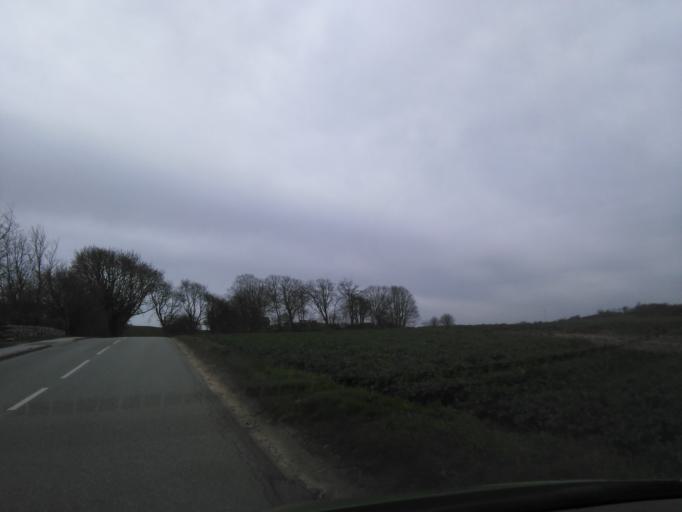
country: DK
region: Central Jutland
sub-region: Arhus Kommune
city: Beder
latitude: 56.0379
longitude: 10.2365
